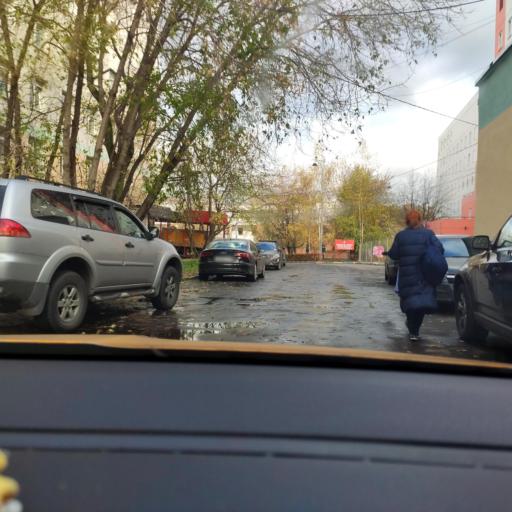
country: RU
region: Moscow
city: Lefortovo
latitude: 55.7677
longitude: 37.7026
